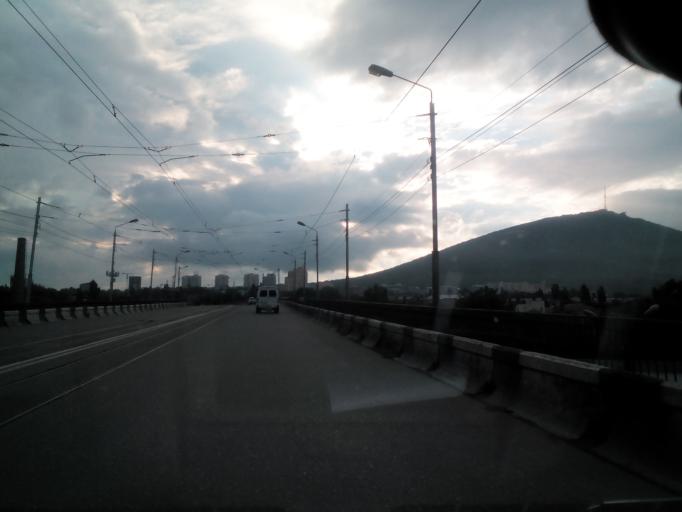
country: RU
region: Stavropol'skiy
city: Pyatigorsk
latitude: 44.0508
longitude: 43.0528
